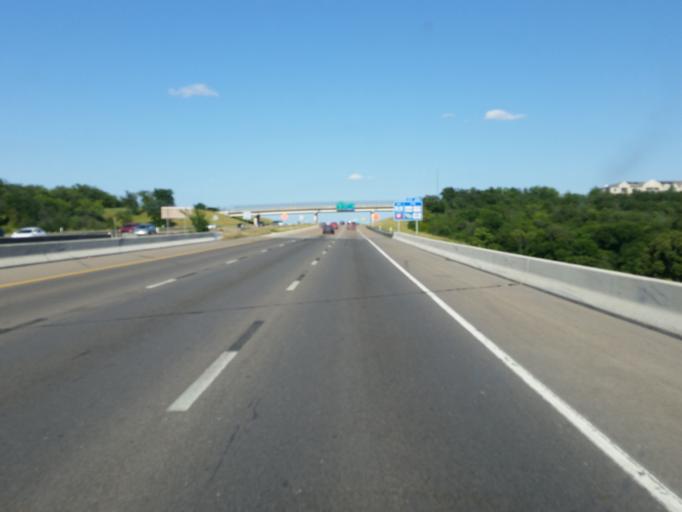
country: US
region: Texas
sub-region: Tarrant County
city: Benbrook
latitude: 32.6836
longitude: -97.4252
